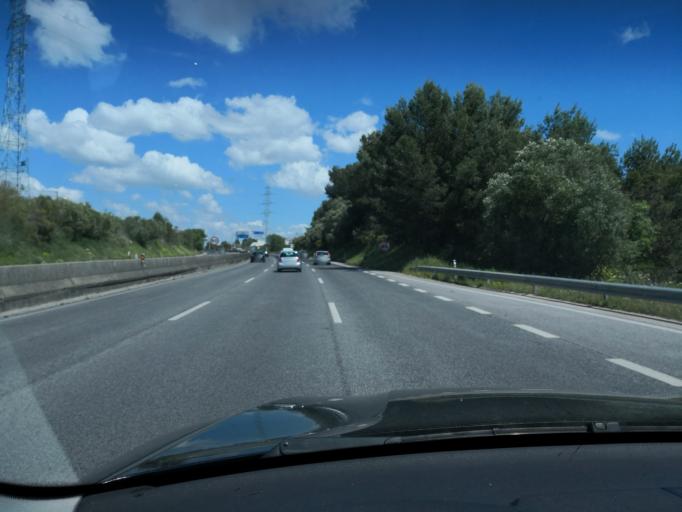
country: PT
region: Setubal
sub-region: Almada
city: Caparica
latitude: 38.6542
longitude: -9.2110
